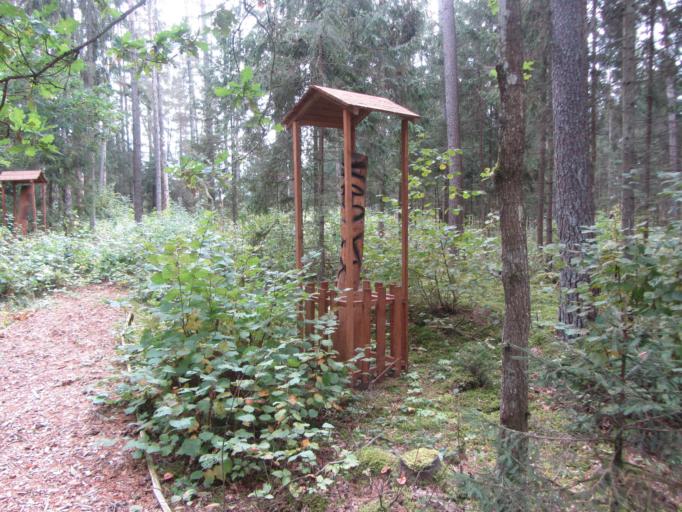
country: LT
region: Alytaus apskritis
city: Druskininkai
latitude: 54.1865
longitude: 24.0692
